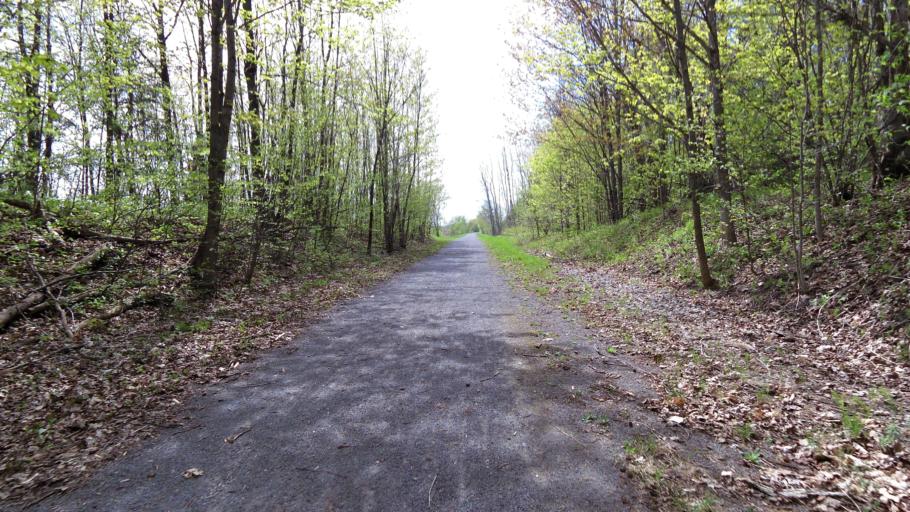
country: CA
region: Ontario
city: Clarence-Rockland
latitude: 45.4148
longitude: -75.4128
